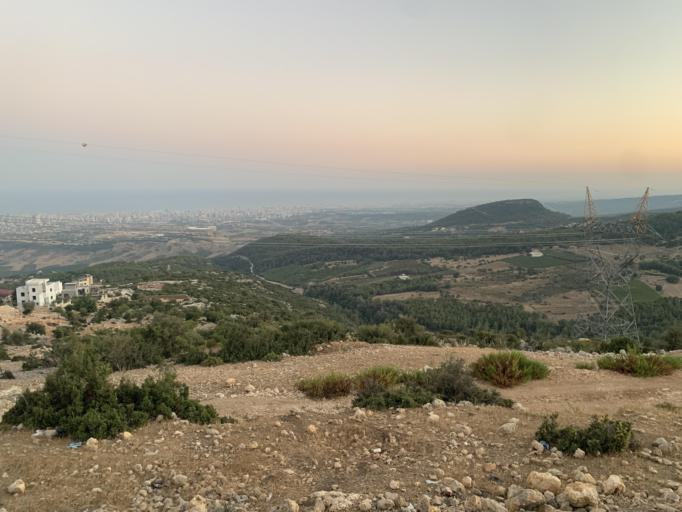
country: TR
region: Mersin
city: Kuzucubelen
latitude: 36.8573
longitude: 34.5259
